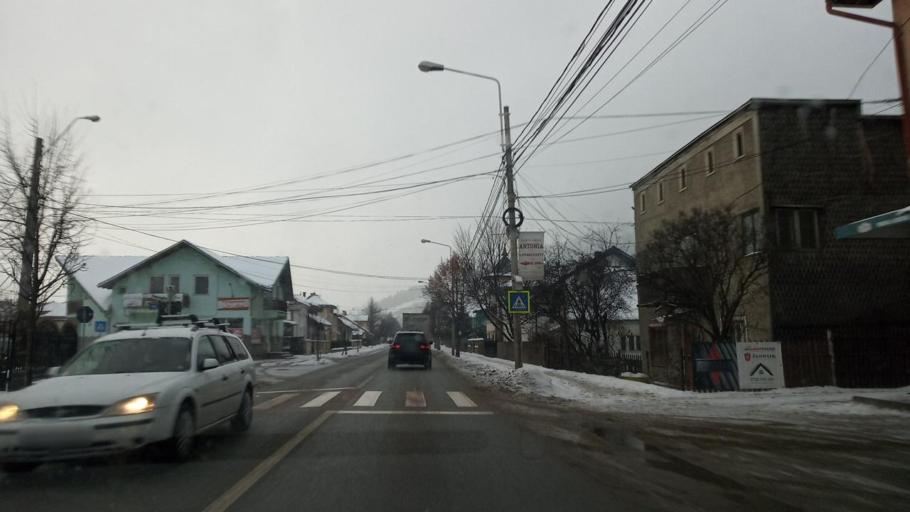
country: RO
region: Suceava
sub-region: Municipiul Vatra Dornei
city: Vatra Dornei
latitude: 47.3465
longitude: 25.3451
